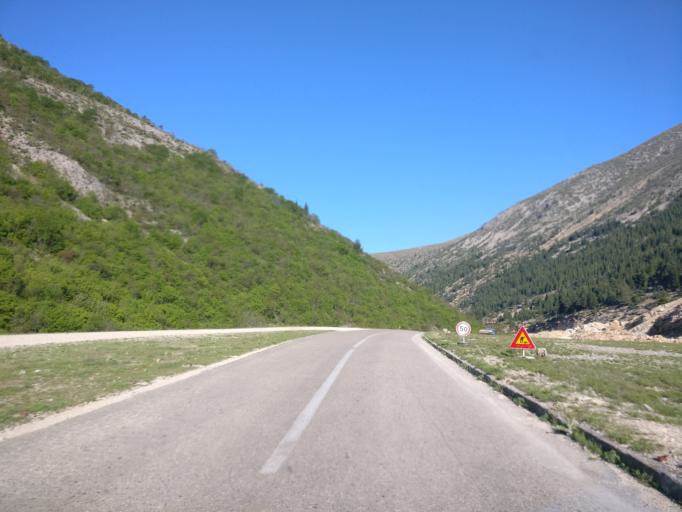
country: BA
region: Federation of Bosnia and Herzegovina
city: Stolac
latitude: 43.0950
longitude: 17.9917
